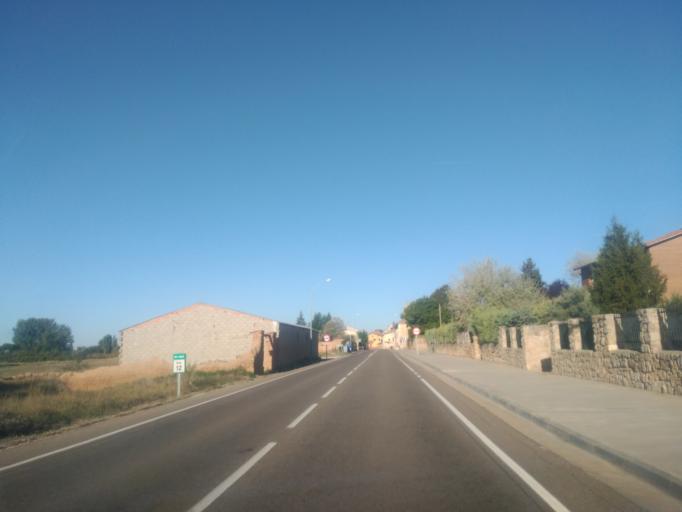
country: ES
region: Castille and Leon
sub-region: Provincia de Burgos
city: Zazuar
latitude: 41.6944
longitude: -3.5498
